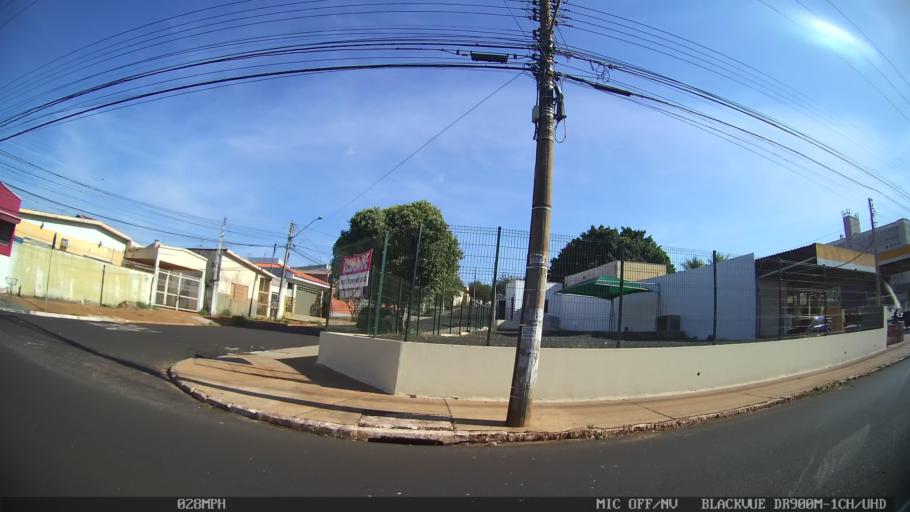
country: BR
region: Sao Paulo
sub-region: Ribeirao Preto
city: Ribeirao Preto
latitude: -21.1766
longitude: -47.7816
